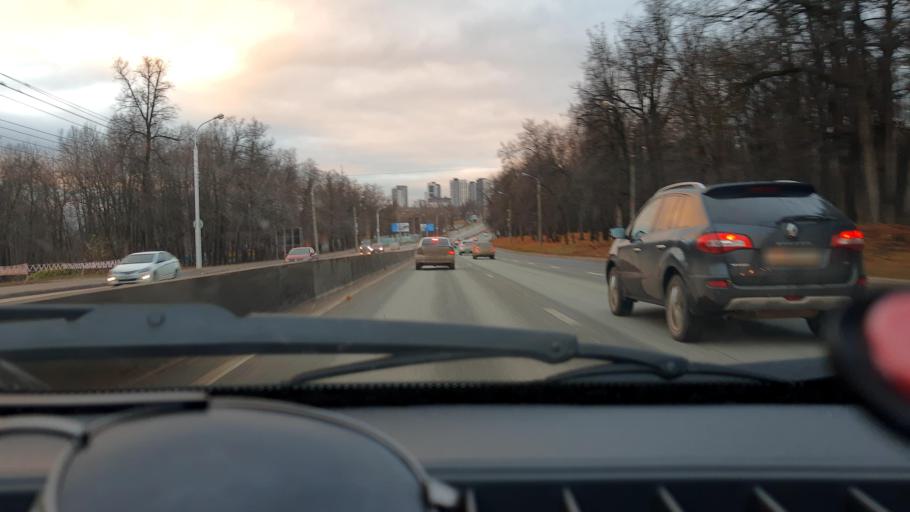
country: RU
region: Bashkortostan
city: Ufa
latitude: 54.7353
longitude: 56.0267
